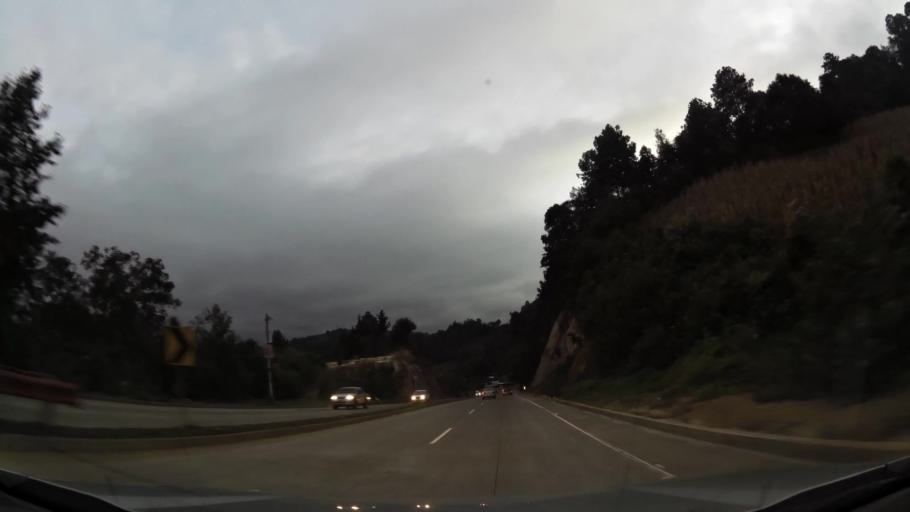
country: GT
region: Chimaltenango
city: Santa Apolonia
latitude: 14.8539
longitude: -91.0507
